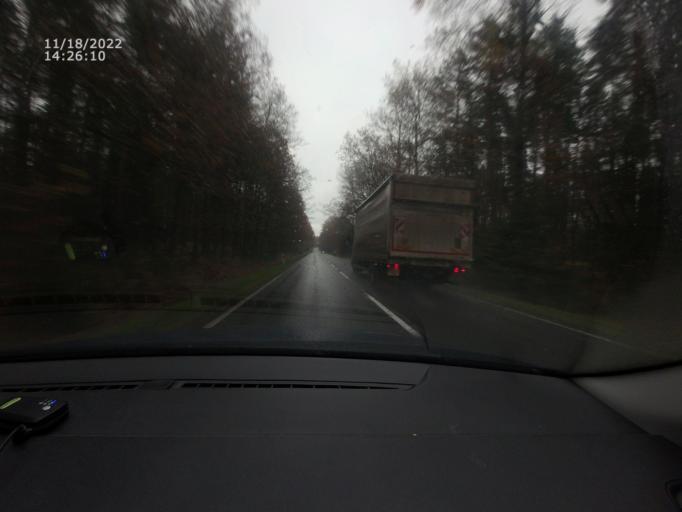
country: CZ
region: Jihocesky
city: Cimelice
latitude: 49.4324
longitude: 14.1678
